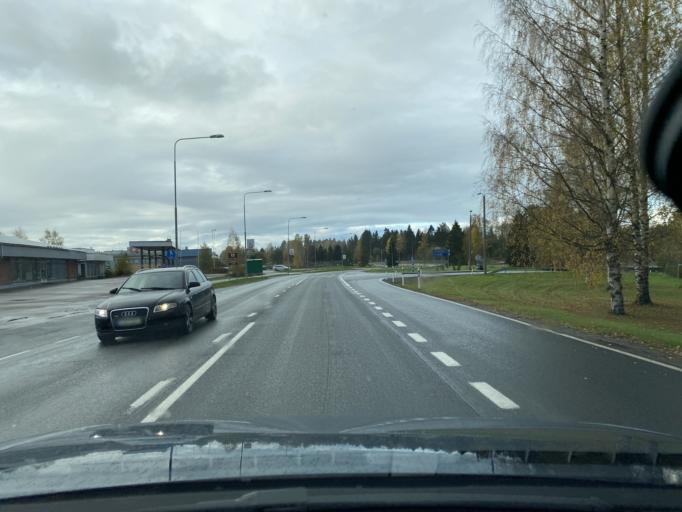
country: FI
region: Haeme
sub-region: Forssa
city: Forssa
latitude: 60.8240
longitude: 23.6004
